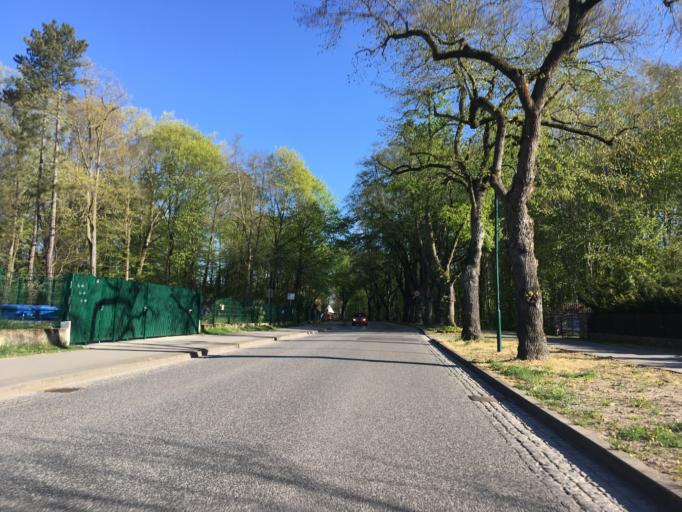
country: DE
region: Berlin
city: Buch
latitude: 52.6643
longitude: 13.5301
